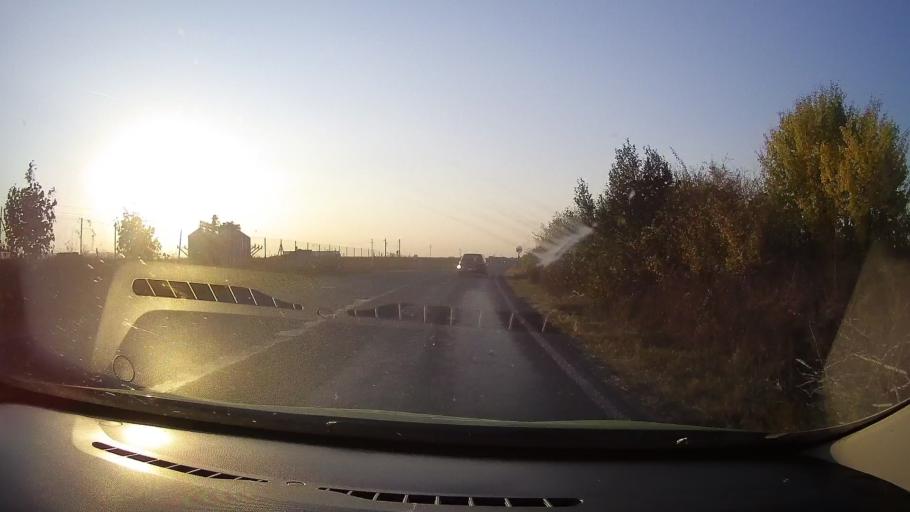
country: RO
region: Arad
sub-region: Comuna Bocsig
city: Bocsig
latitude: 46.4193
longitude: 21.9632
